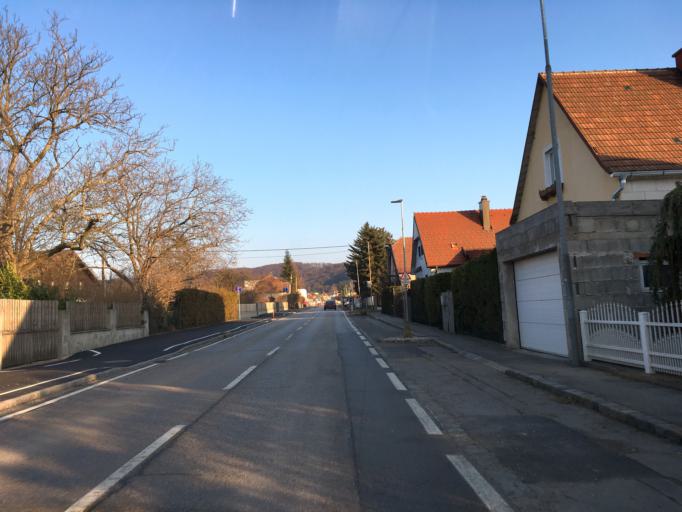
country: AT
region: Lower Austria
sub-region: Politischer Bezirk Tulln
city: Wordern
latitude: 48.3233
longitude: 16.1940
